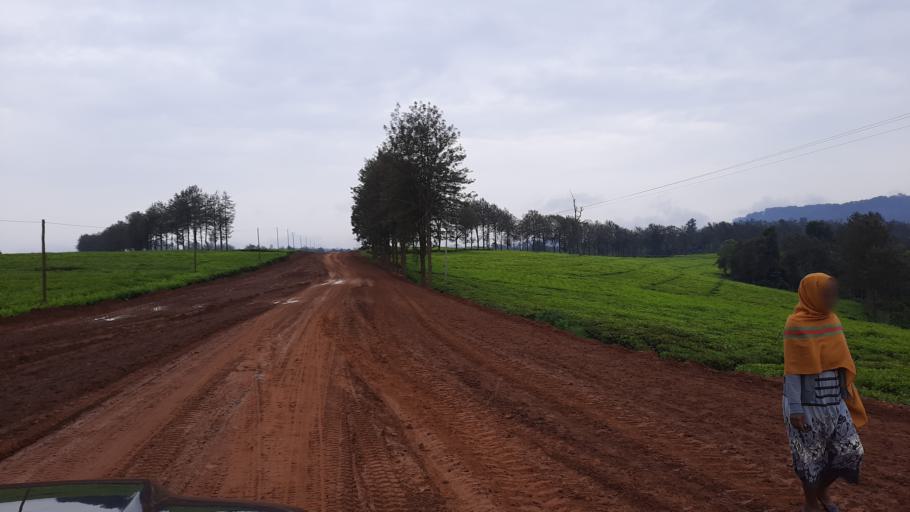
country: ET
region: Oromiya
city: Gore
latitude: 7.8490
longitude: 35.4763
